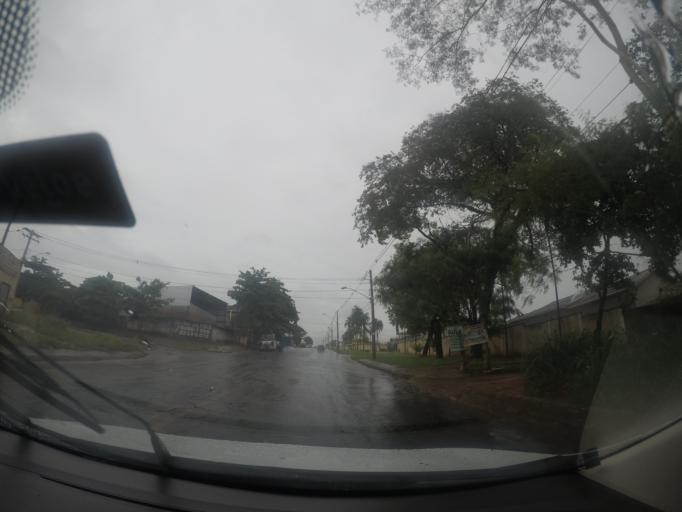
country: BR
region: Goias
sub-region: Goiania
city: Goiania
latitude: -16.6607
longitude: -49.3171
